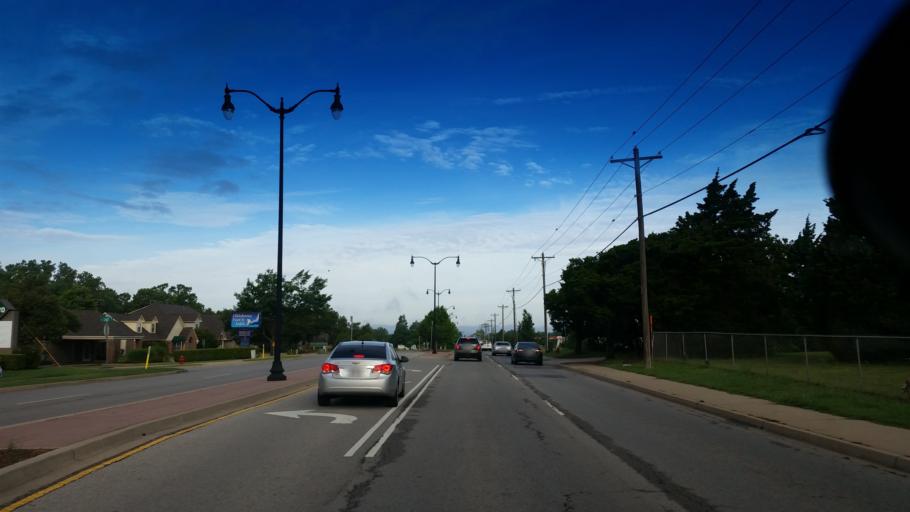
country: US
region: Oklahoma
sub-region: Oklahoma County
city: Edmond
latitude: 35.6384
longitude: -97.4917
